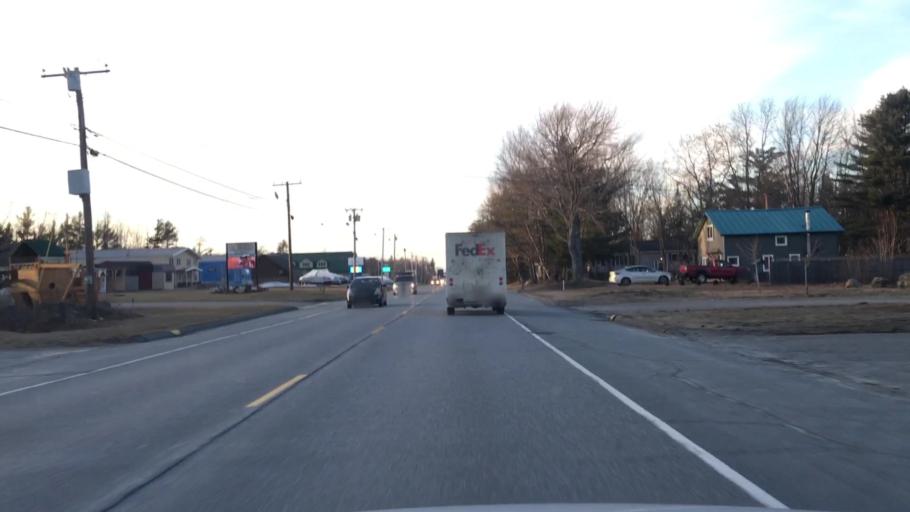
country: US
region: Maine
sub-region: Penobscot County
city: Holden
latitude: 44.7589
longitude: -68.6920
